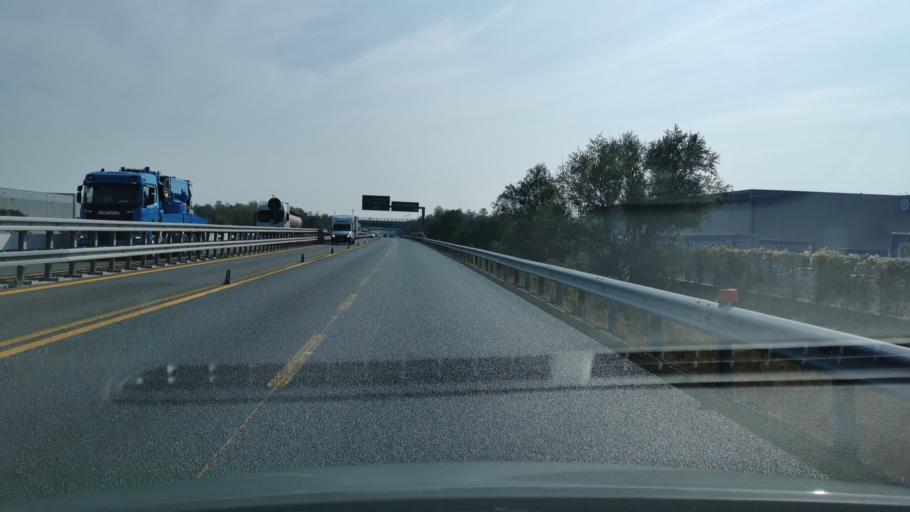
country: IT
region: Emilia-Romagna
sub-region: Provincia di Piacenza
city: Castel San Giovanni
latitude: 45.0765
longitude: 9.4436
